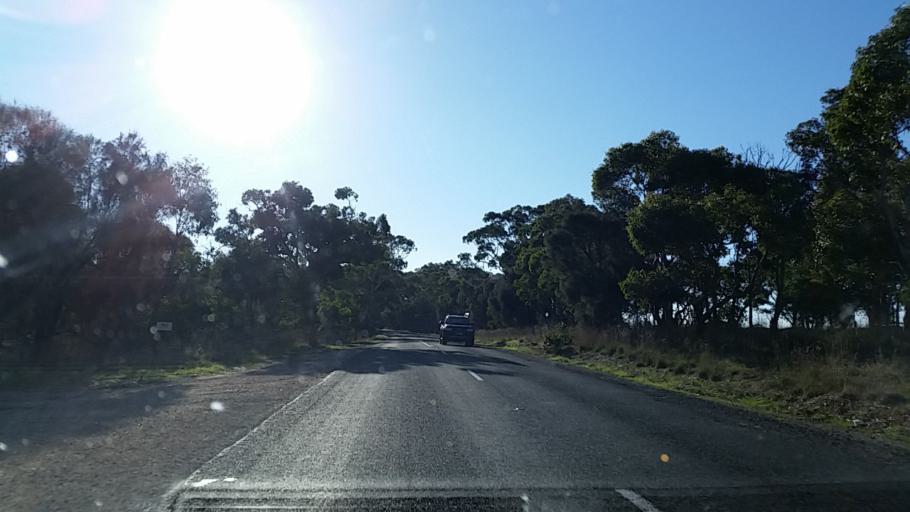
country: AU
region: South Australia
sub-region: Mount Barker
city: Macclesfield
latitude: -35.1400
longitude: 138.9199
